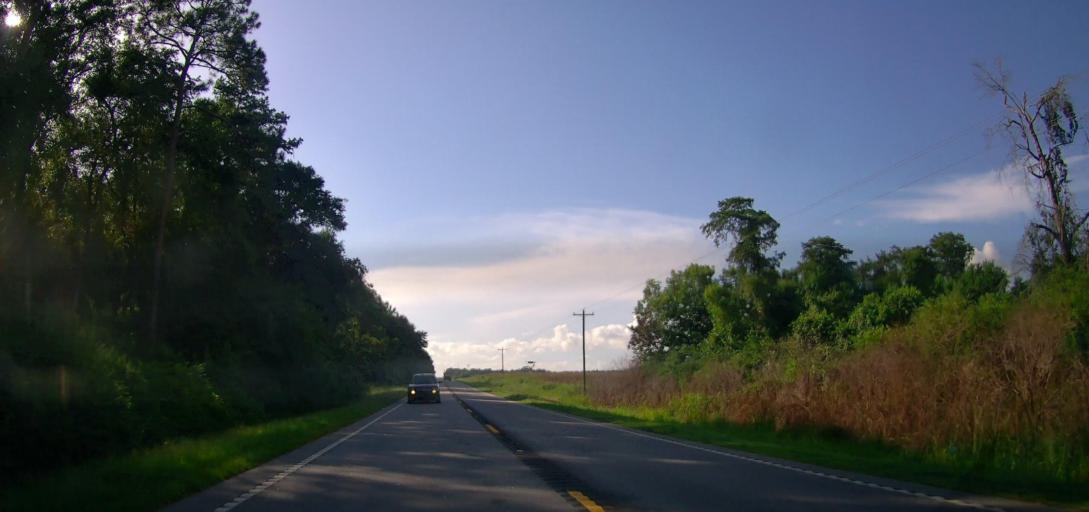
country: US
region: Georgia
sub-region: Coffee County
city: Nicholls
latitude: 31.4324
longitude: -82.7061
